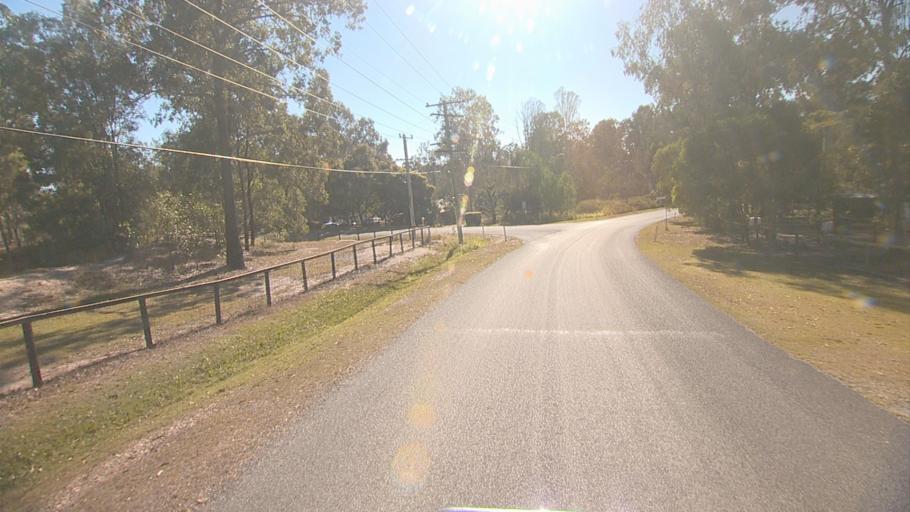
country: AU
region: Queensland
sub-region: Logan
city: Chambers Flat
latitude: -27.7885
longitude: 153.1316
